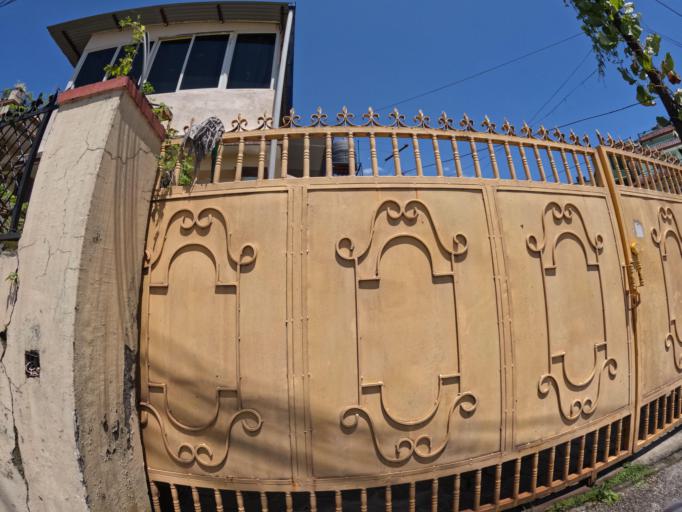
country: NP
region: Central Region
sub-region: Bagmati Zone
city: Kathmandu
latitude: 27.7438
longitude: 85.3255
